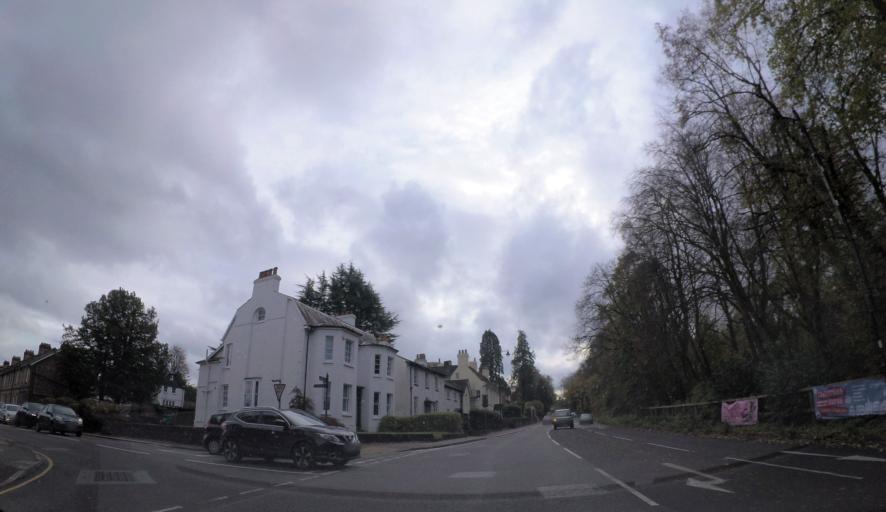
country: GB
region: England
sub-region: Surrey
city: Reigate
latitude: 51.2343
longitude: -0.2037
